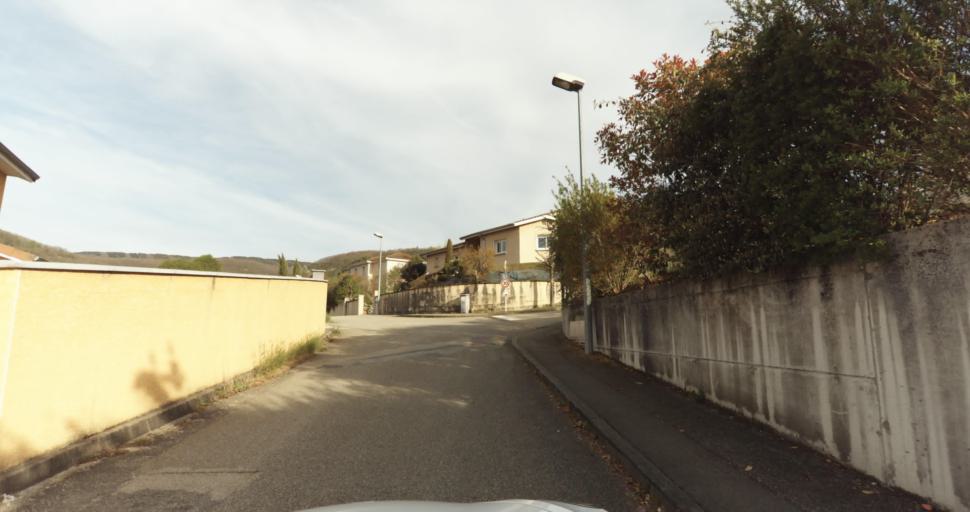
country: FR
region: Rhone-Alpes
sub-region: Departement de l'Ain
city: Amberieu-en-Bugey
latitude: 45.9553
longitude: 5.3667
